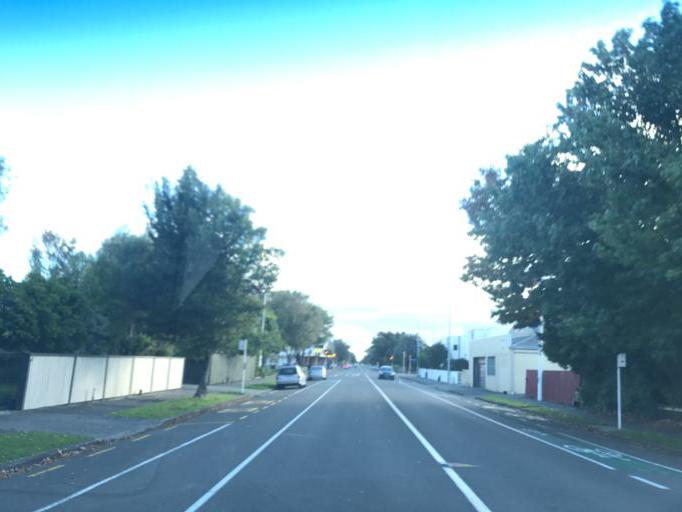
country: NZ
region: Manawatu-Wanganui
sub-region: Palmerston North City
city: Palmerston North
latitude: -40.3617
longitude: 175.6172
